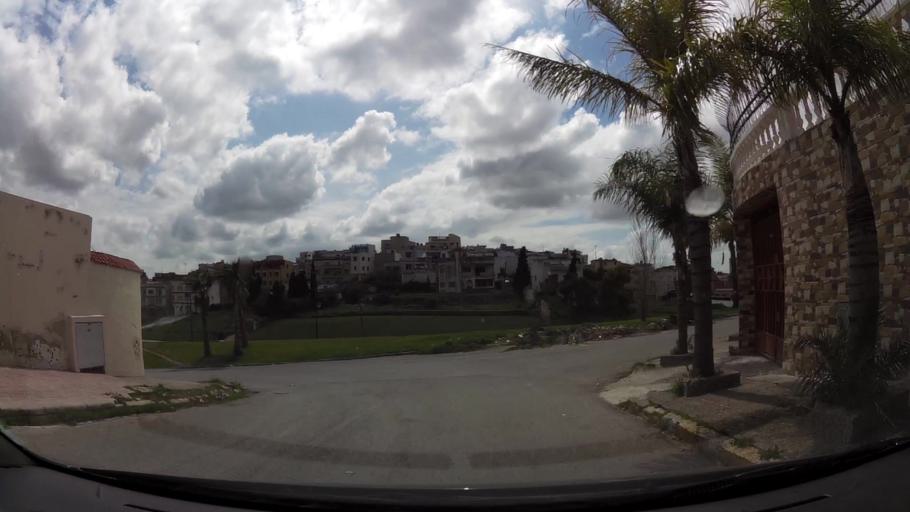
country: MA
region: Tanger-Tetouan
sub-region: Tanger-Assilah
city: Tangier
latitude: 35.7733
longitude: -5.7730
